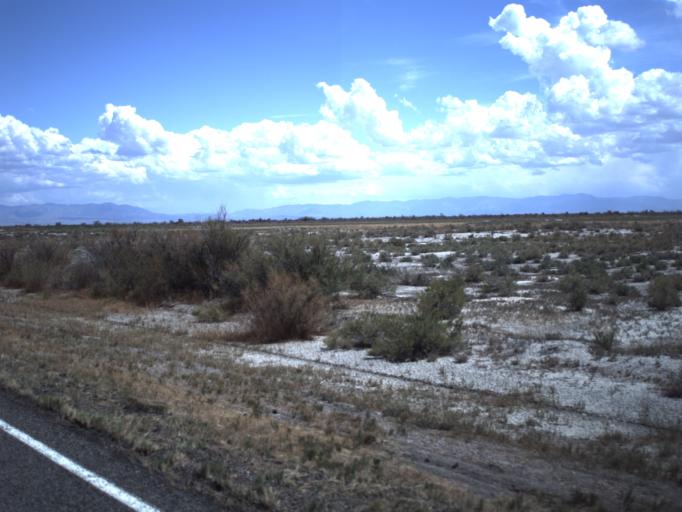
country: US
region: Utah
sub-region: Millard County
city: Delta
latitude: 39.3051
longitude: -112.8015
